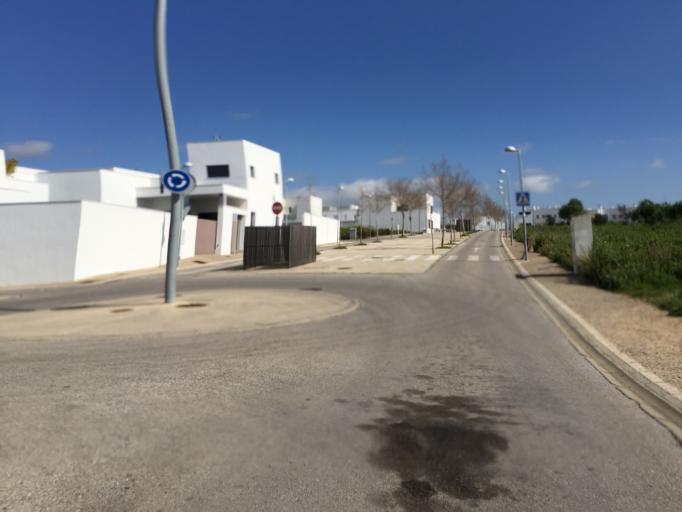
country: ES
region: Andalusia
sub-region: Provincia de Cadiz
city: Conil de la Frontera
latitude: 36.2839
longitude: -6.0813
